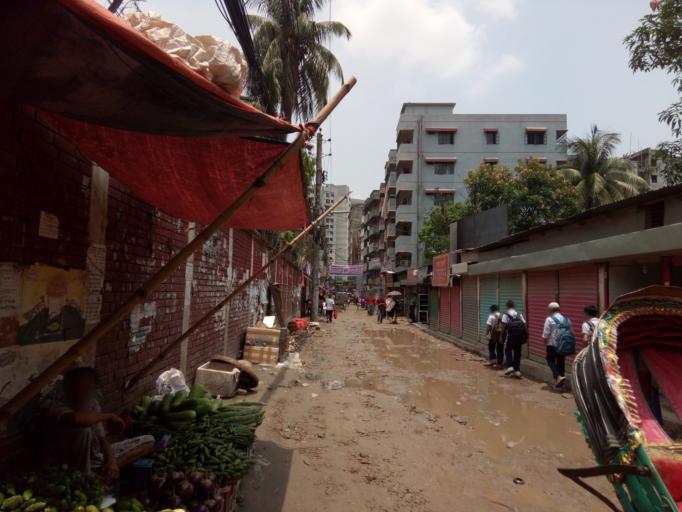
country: BD
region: Dhaka
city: Paltan
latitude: 23.7650
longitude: 90.4222
